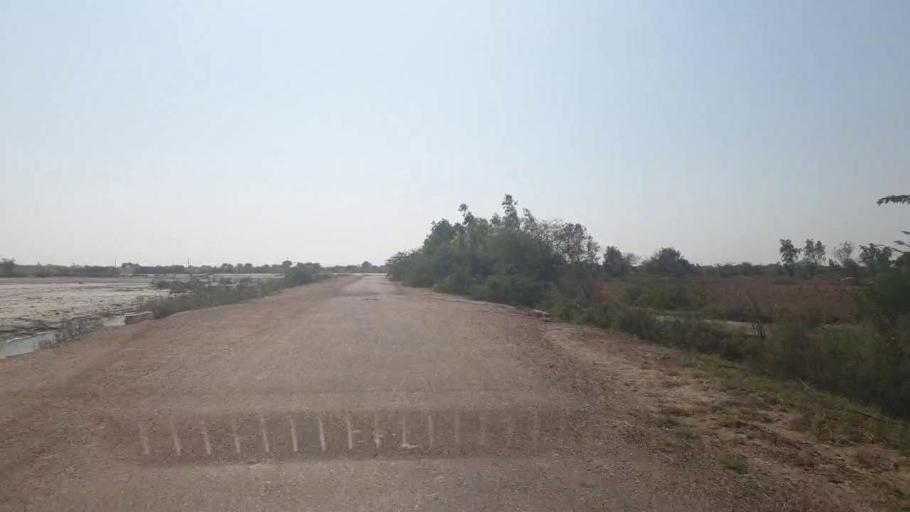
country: PK
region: Sindh
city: Badin
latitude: 24.5555
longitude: 68.8377
